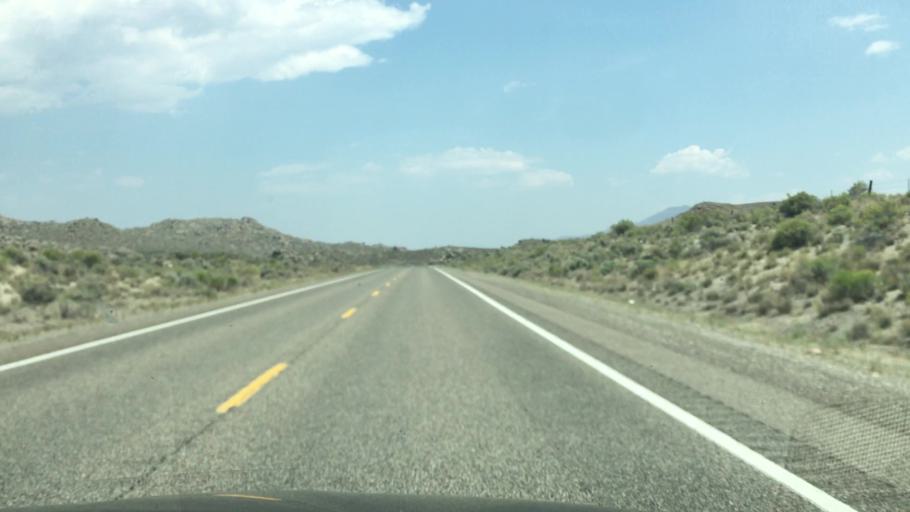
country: US
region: Nevada
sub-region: Elko County
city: Jackpot
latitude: 41.7323
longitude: -114.7914
